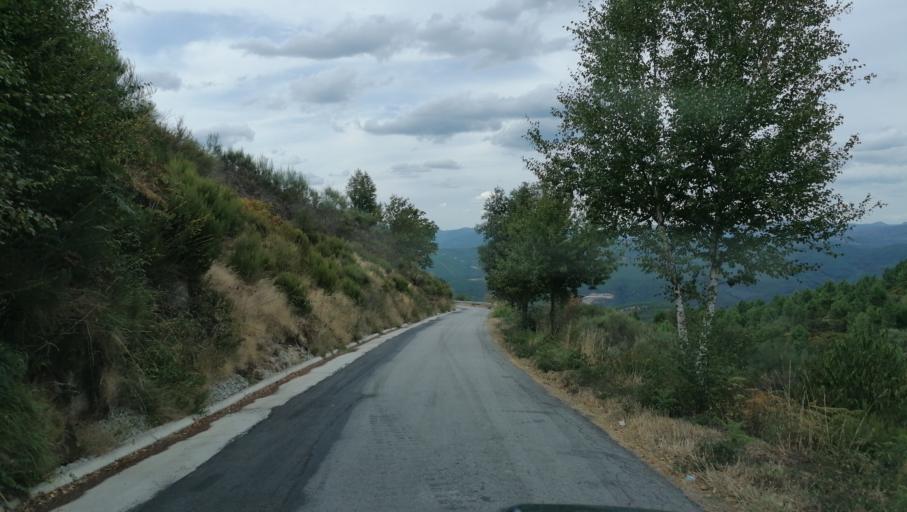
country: PT
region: Vila Real
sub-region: Vila Pouca de Aguiar
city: Vila Pouca de Aguiar
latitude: 41.5556
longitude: -7.7007
